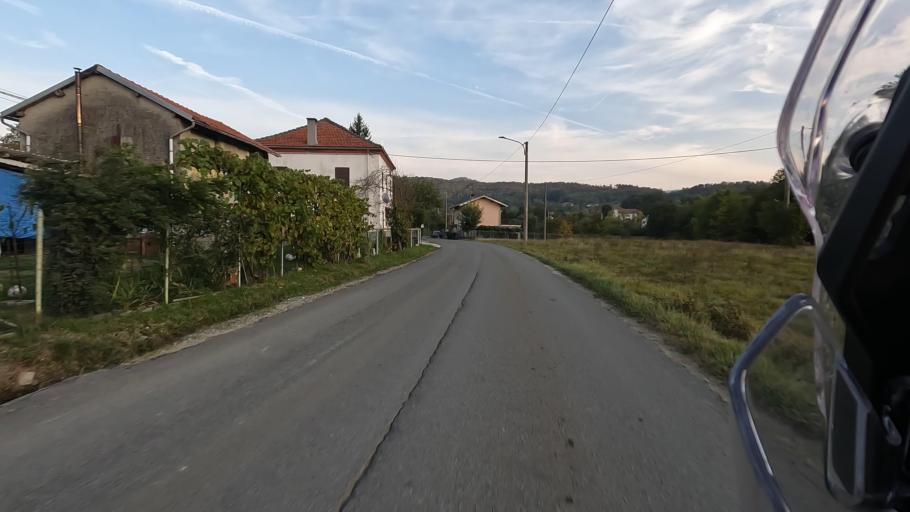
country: IT
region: Liguria
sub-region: Provincia di Savona
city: Mioglia
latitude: 44.4734
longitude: 8.4151
